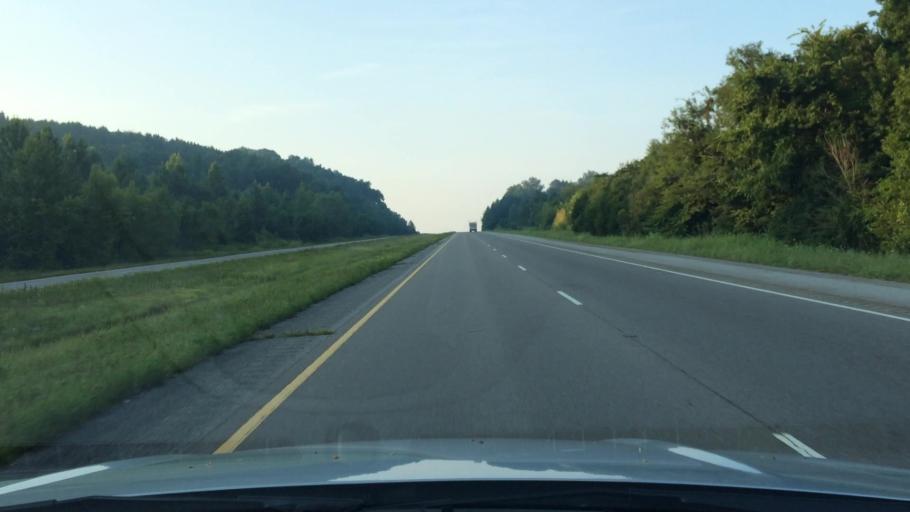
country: US
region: Tennessee
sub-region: Giles County
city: Pulaski
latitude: 35.1837
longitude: -87.0627
